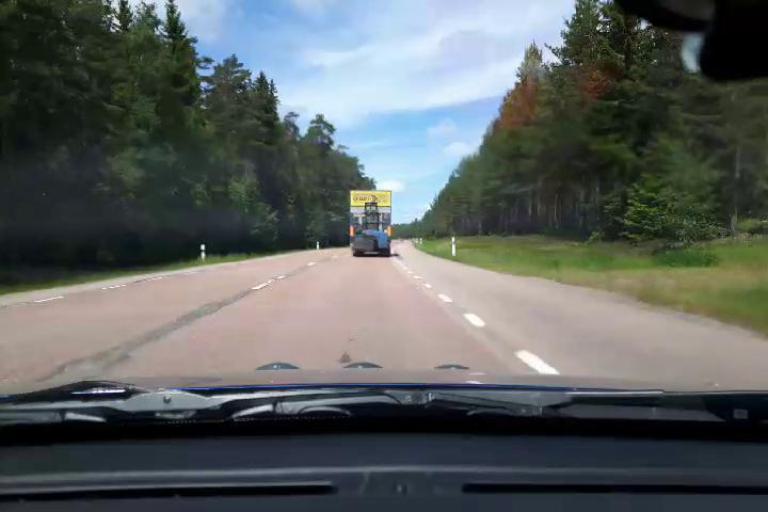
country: SE
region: Uppsala
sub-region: Osthammars Kommun
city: Bjorklinge
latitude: 60.1252
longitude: 17.5092
